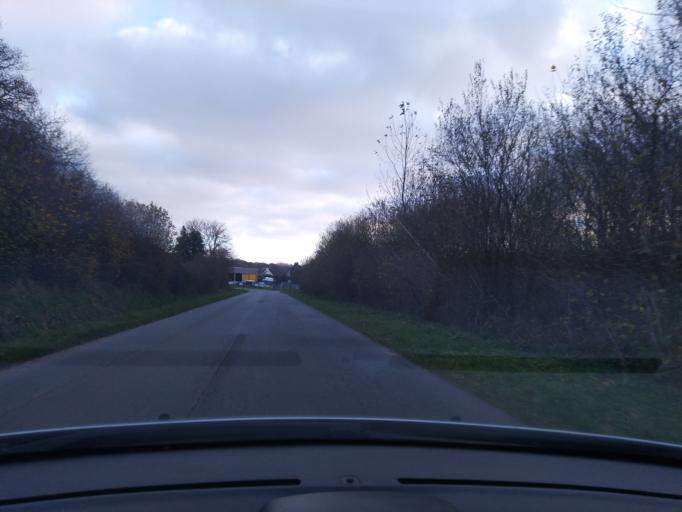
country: FR
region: Brittany
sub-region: Departement du Finistere
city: Guerlesquin
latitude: 48.5210
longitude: -3.5865
